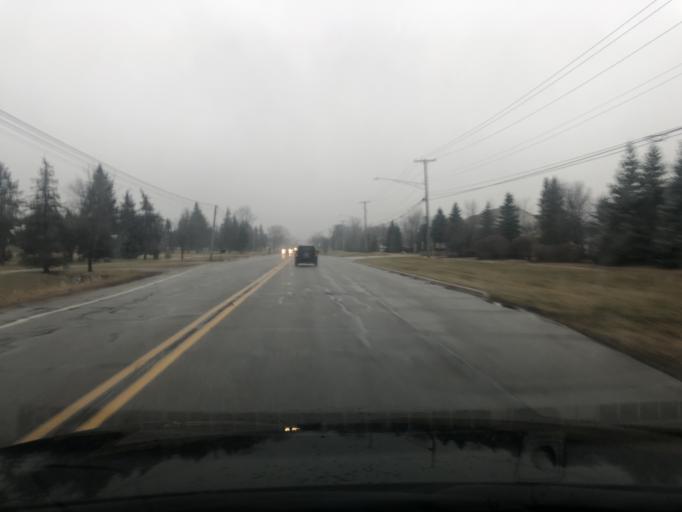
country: US
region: Michigan
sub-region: Wayne County
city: Woodhaven
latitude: 42.1174
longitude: -83.2254
